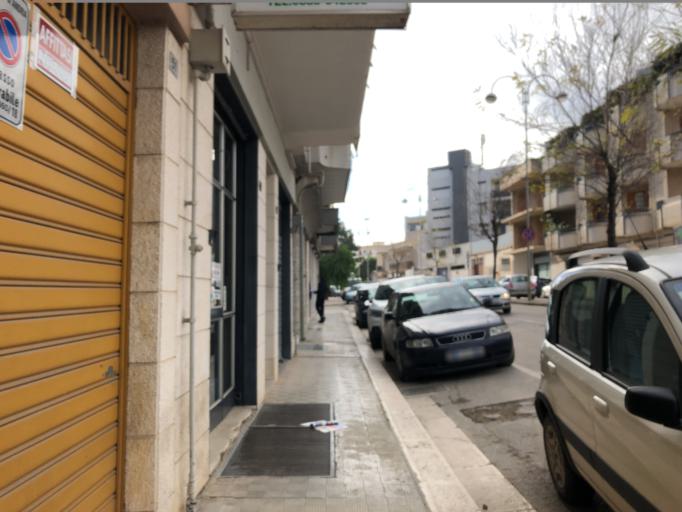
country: IT
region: Apulia
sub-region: Provincia di Barletta - Andria - Trani
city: Andria
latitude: 41.2203
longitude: 16.3064
